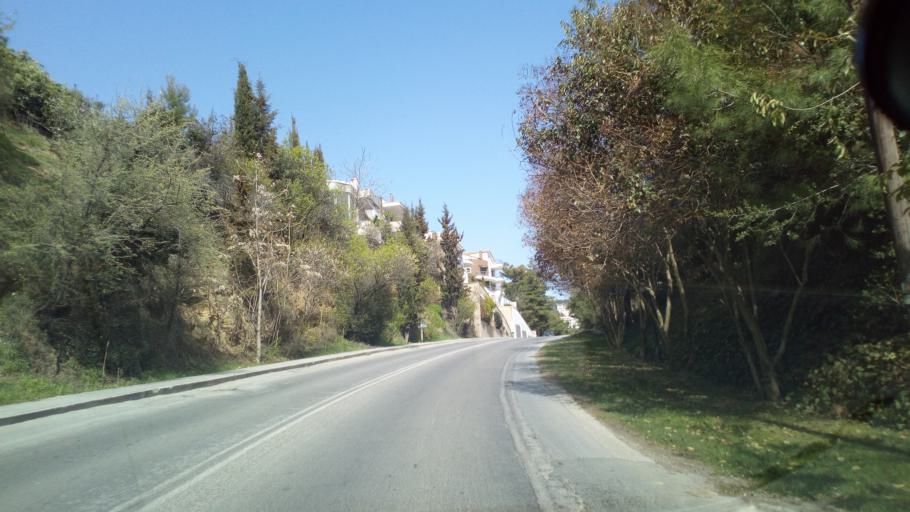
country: GR
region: Central Macedonia
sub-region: Nomos Thessalonikis
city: Panorama
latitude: 40.5775
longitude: 23.0261
